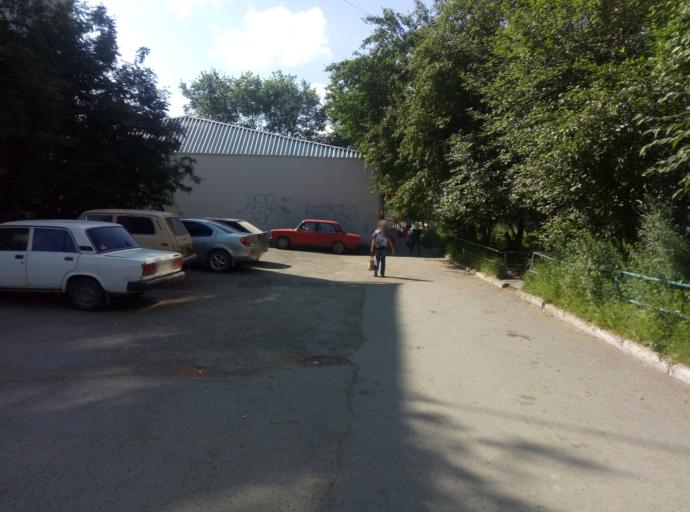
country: RU
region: Sverdlovsk
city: Krasnotur'insk
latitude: 59.7643
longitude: 60.2075
